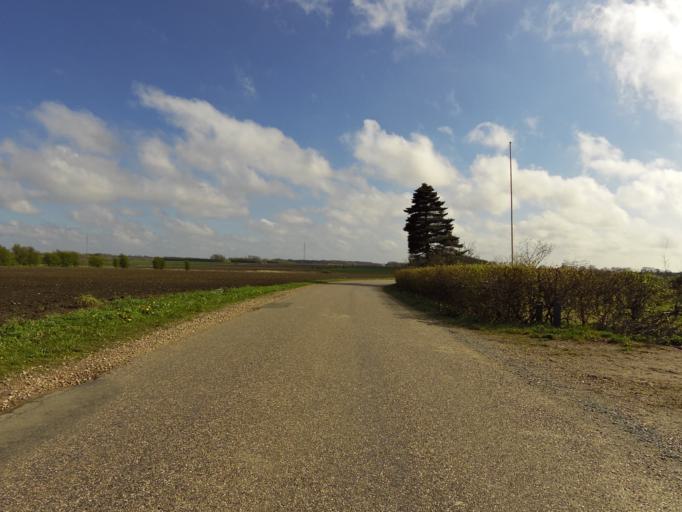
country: DK
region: South Denmark
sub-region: Vejen Kommune
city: Rodding
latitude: 55.3489
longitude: 8.9908
